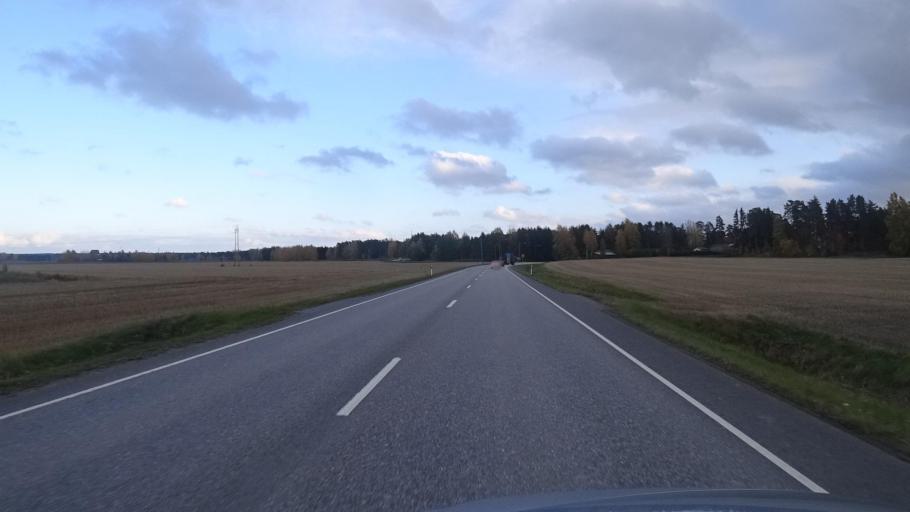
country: FI
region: Satakunta
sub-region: Rauma
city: Saekylae
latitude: 61.0405
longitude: 22.3806
